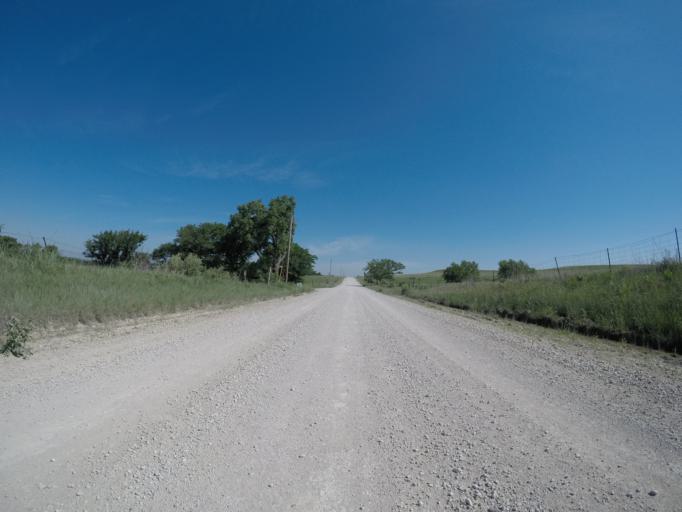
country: US
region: Kansas
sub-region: Wabaunsee County
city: Alma
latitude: 39.0005
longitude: -96.1138
